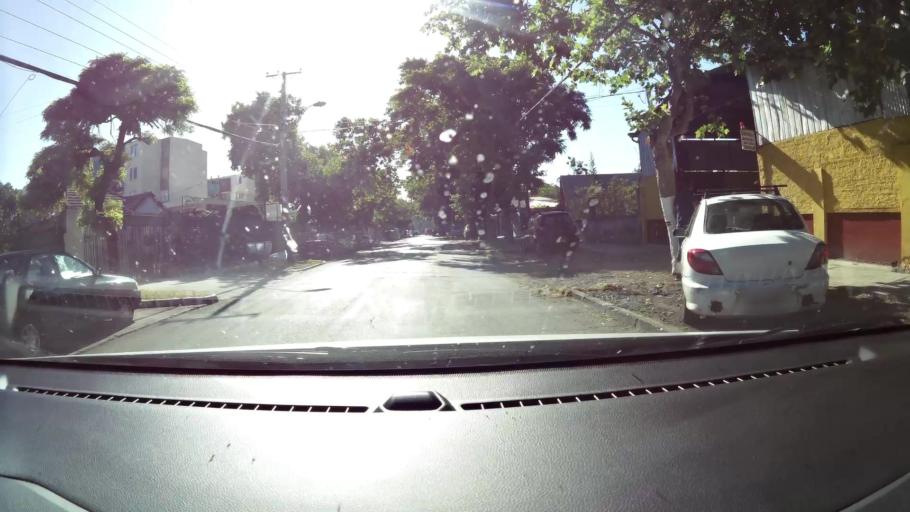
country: CL
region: Santiago Metropolitan
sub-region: Provincia de Maipo
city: San Bernardo
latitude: -33.5509
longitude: -70.6742
